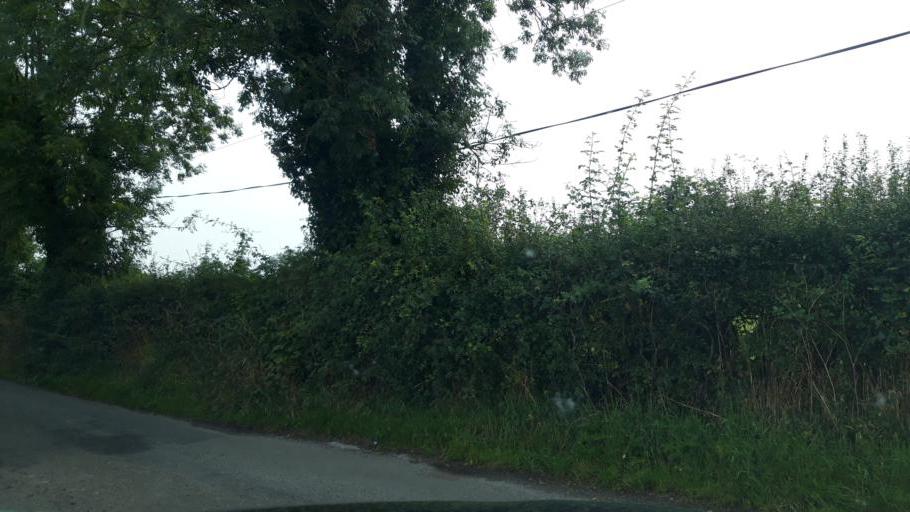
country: IE
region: Leinster
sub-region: Kilkenny
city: Callan
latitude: 52.5511
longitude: -7.3903
